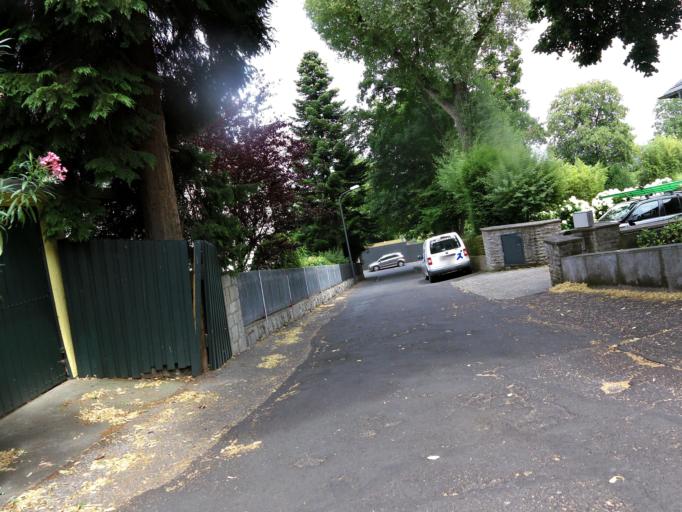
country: DE
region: Bavaria
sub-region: Regierungsbezirk Unterfranken
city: Wuerzburg
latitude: 49.7719
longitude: 9.9269
